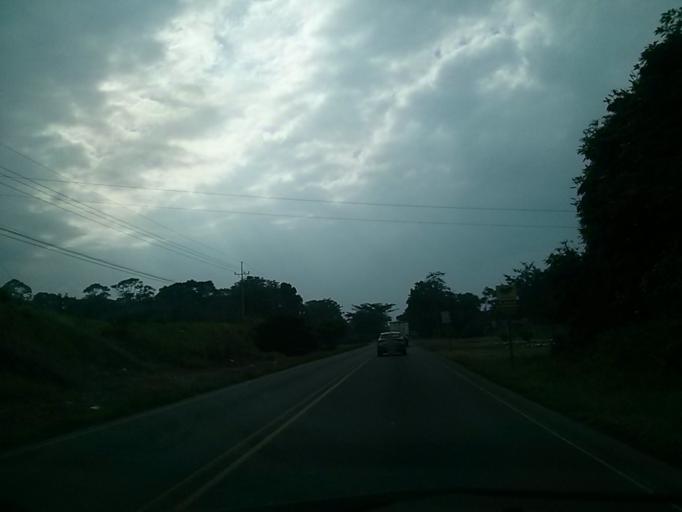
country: CR
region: Limon
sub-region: Canton de Guacimo
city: Guacimo
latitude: 10.2034
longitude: -83.6796
